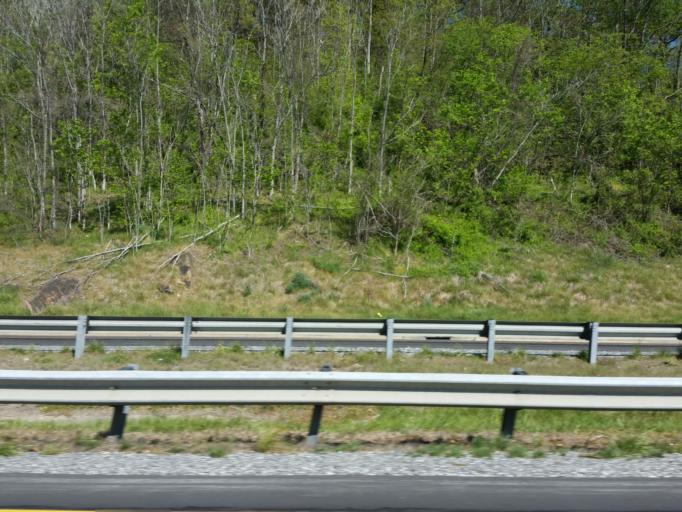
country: US
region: North Carolina
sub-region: Buncombe County
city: Asheville
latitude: 35.6064
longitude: -82.5774
